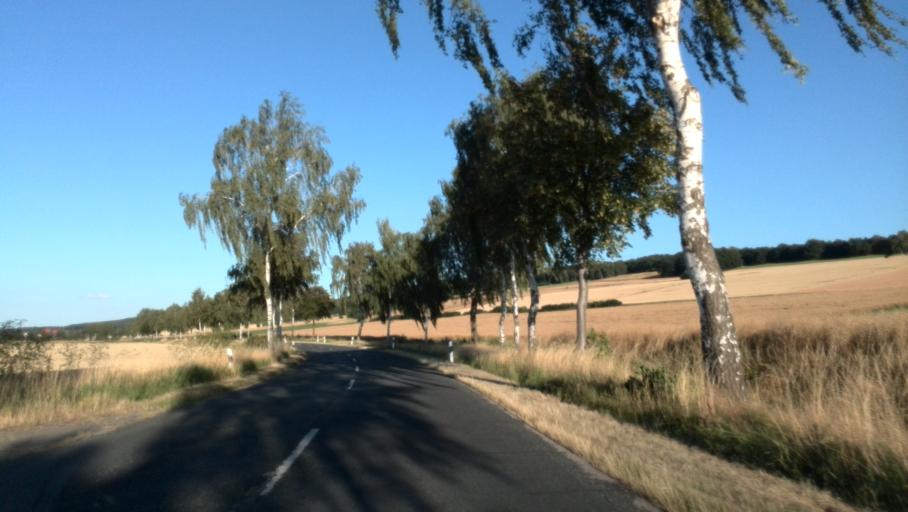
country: DE
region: Lower Saxony
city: Bad Salzdetfurth
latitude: 52.0927
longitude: 10.0486
